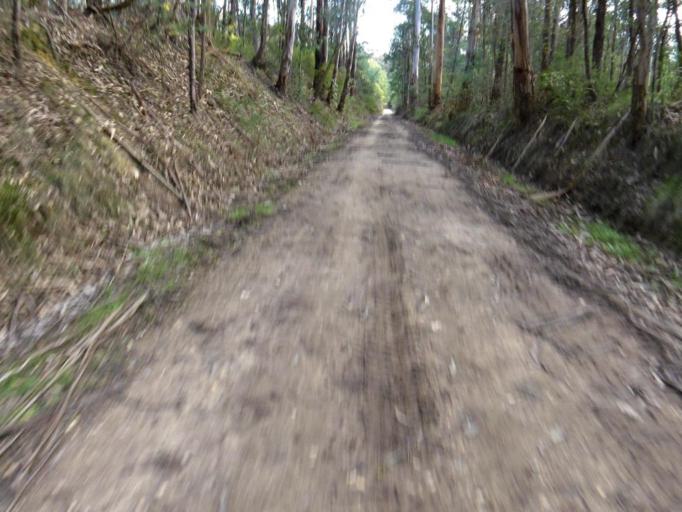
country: AU
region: Victoria
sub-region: Baw Baw
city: Warragul
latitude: -38.0634
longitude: 145.9436
